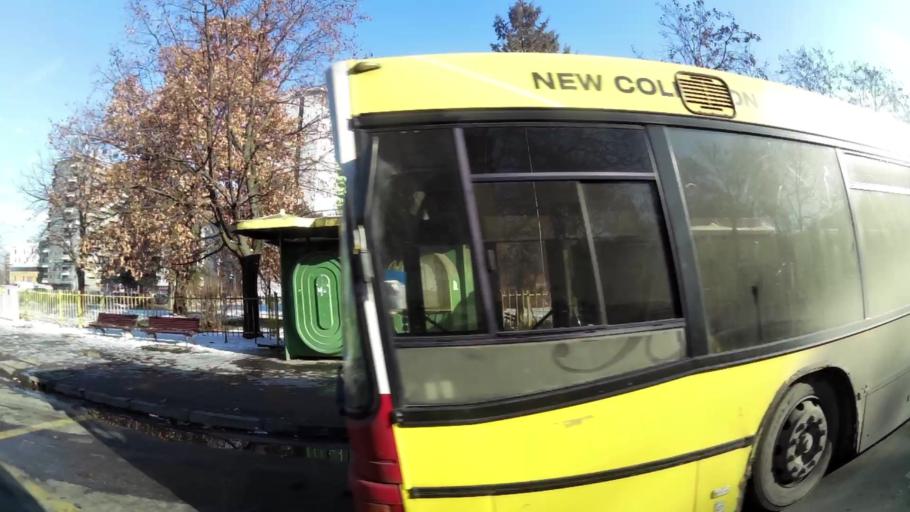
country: MK
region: Karpos
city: Skopje
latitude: 42.0059
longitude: 21.3907
